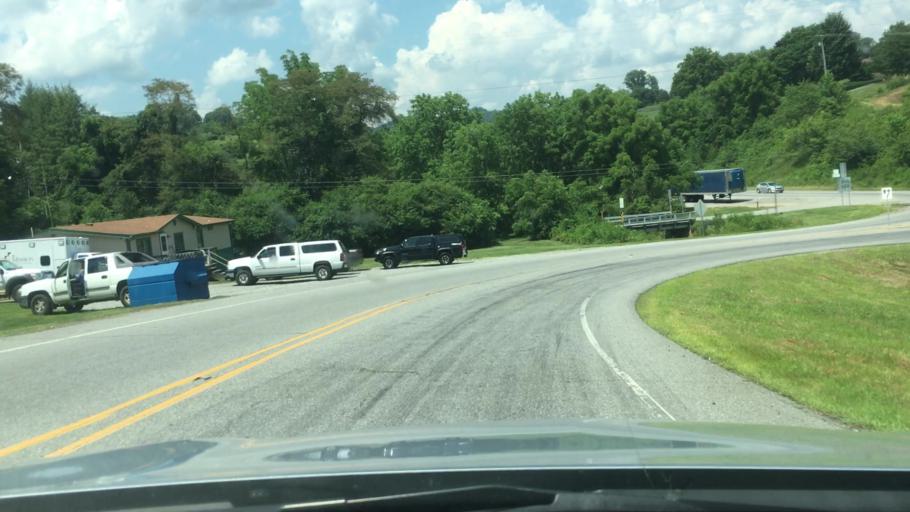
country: US
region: North Carolina
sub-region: Madison County
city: Marshall
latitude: 35.8040
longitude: -82.6591
